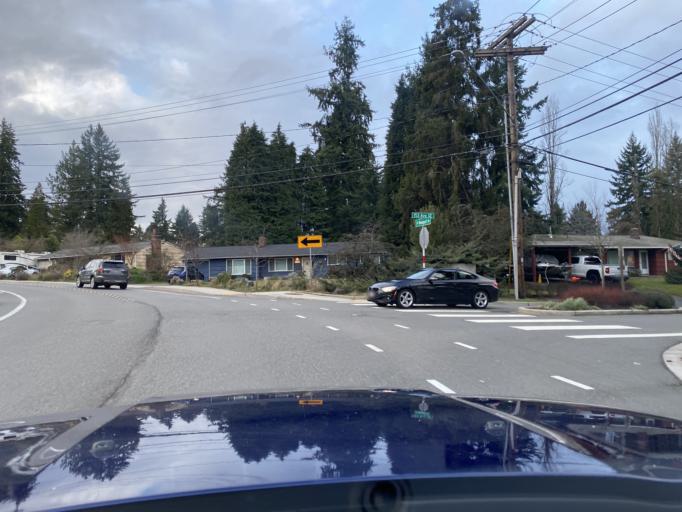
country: US
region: Washington
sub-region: King County
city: Eastgate
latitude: 47.5712
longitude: -122.1375
